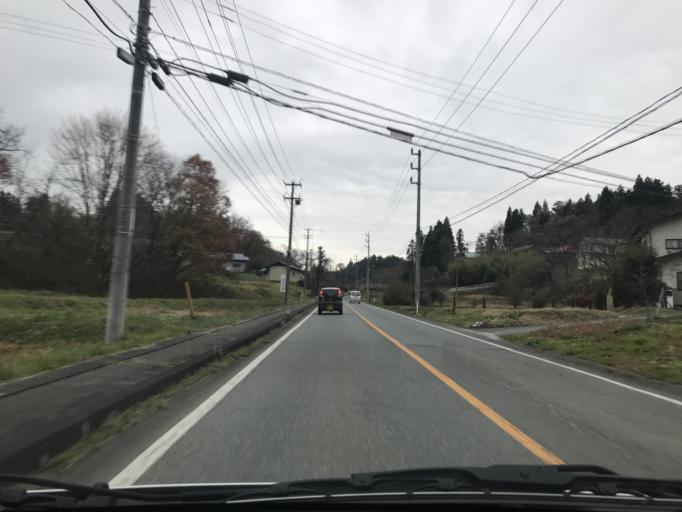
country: JP
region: Iwate
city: Ichinoseki
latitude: 39.0177
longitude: 141.3299
